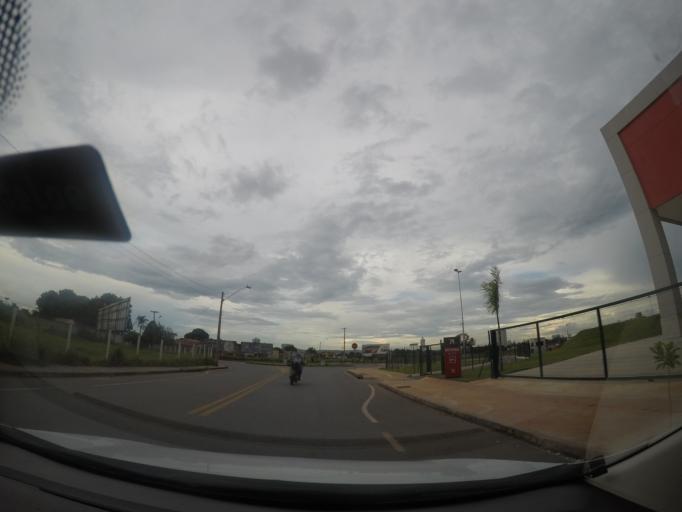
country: BR
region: Goias
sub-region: Goiania
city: Goiania
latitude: -16.6544
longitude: -49.2671
